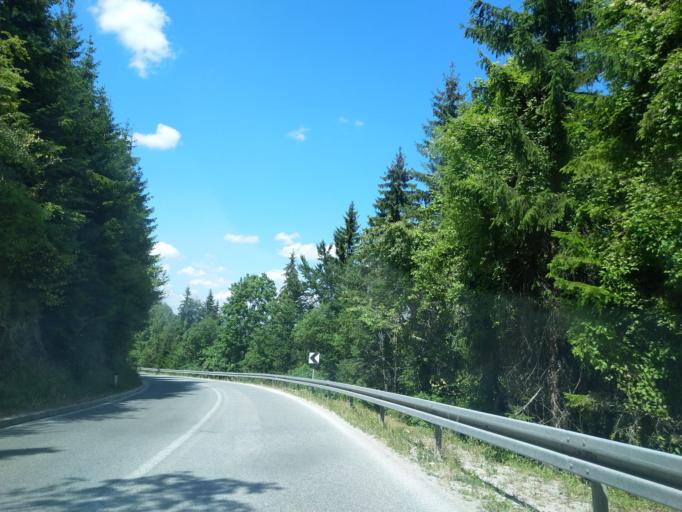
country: RS
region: Central Serbia
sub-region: Zlatiborski Okrug
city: Nova Varos
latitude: 43.4169
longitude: 19.8298
